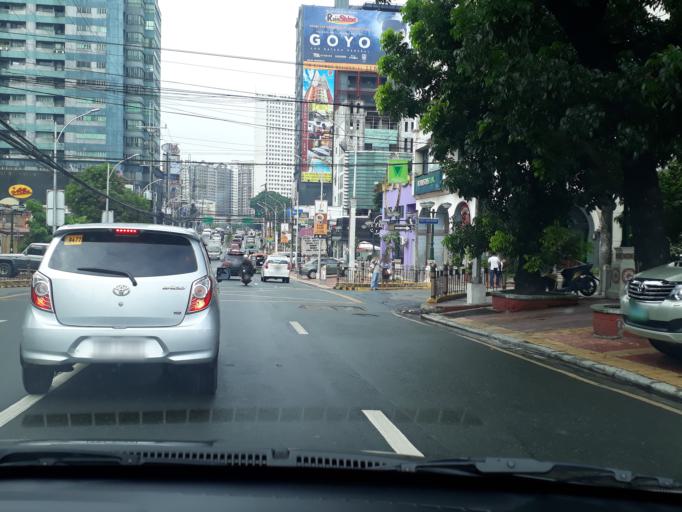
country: PH
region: Calabarzon
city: Del Monte
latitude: 14.6305
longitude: 121.0343
